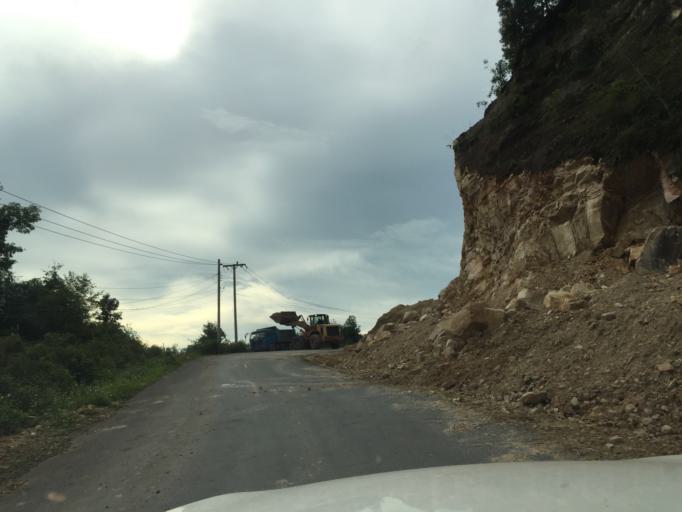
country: LA
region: Phongsali
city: Phongsali
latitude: 21.3128
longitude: 102.0482
